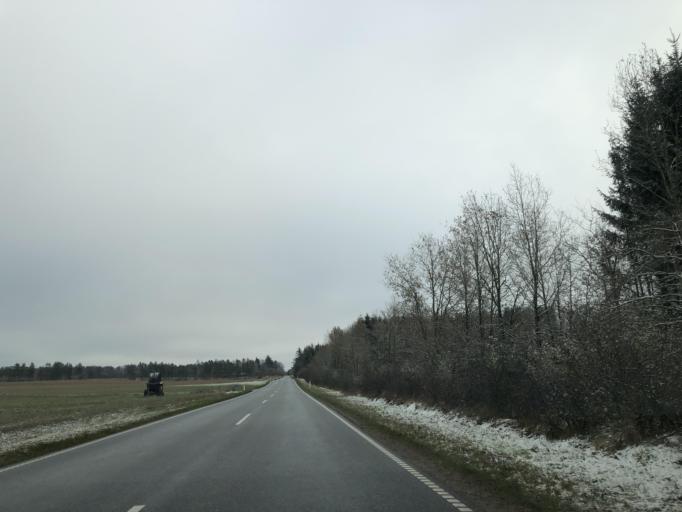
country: DK
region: Central Jutland
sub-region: Ikast-Brande Kommune
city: Brande
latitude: 55.9854
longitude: 9.2531
